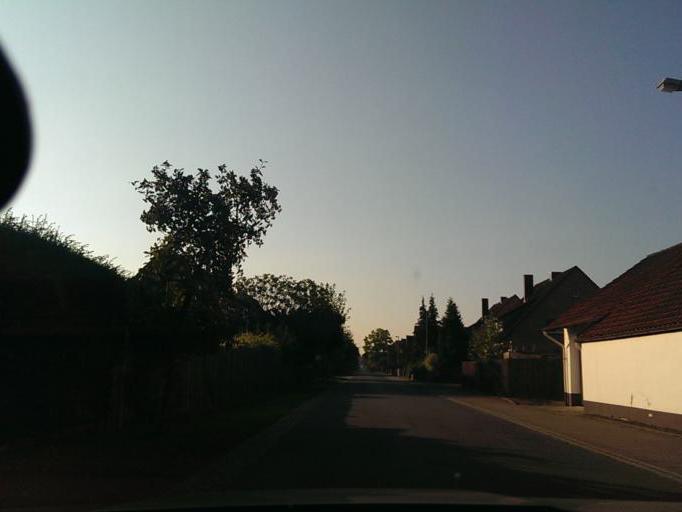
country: DE
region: Lower Saxony
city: Elze
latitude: 52.5797
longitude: 9.7352
